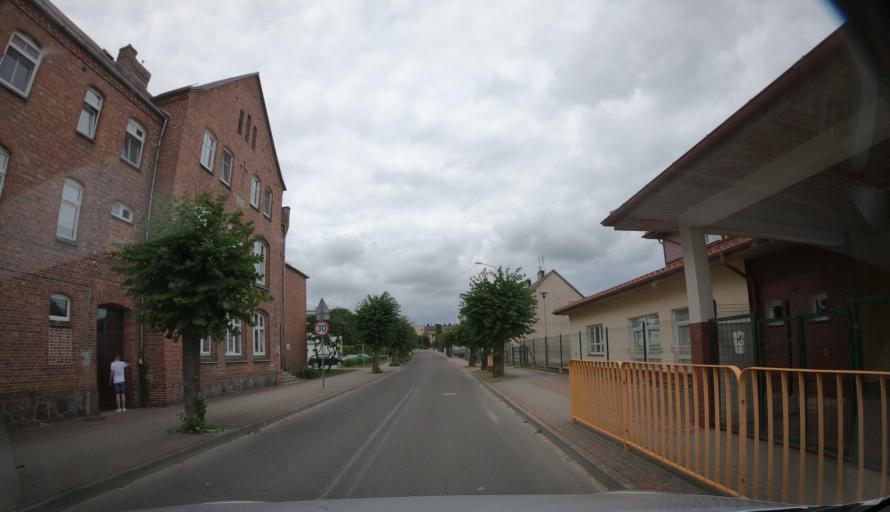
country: PL
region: West Pomeranian Voivodeship
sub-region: Powiat kamienski
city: Golczewo
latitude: 53.8216
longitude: 14.9793
